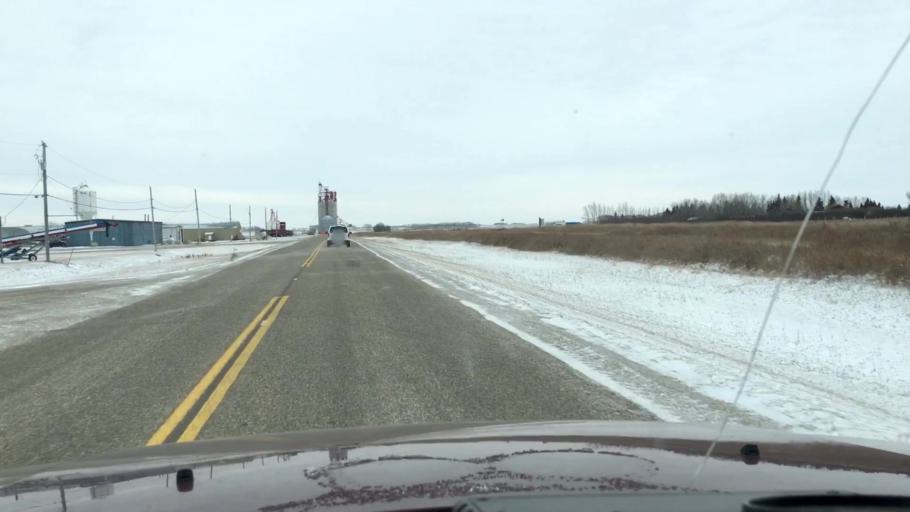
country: CA
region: Saskatchewan
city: Watrous
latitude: 51.2541
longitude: -105.9827
